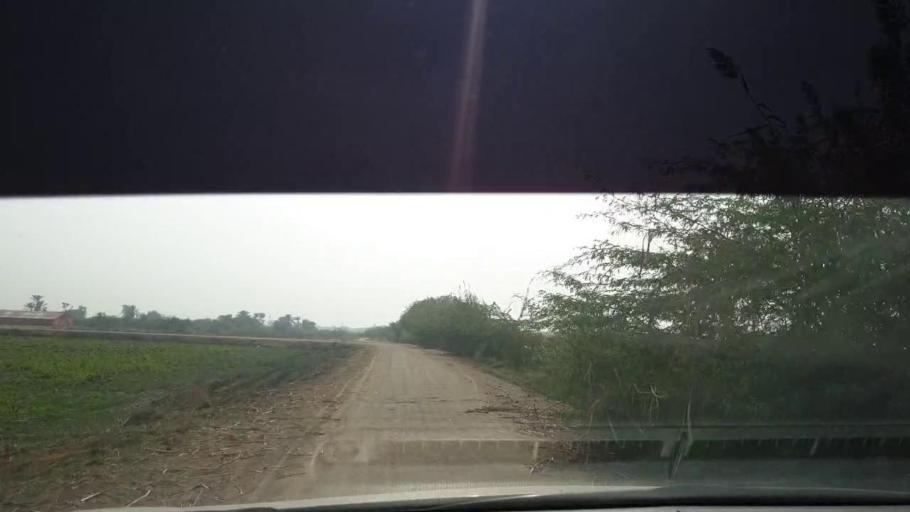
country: PK
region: Sindh
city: Berani
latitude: 25.8293
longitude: 68.8403
